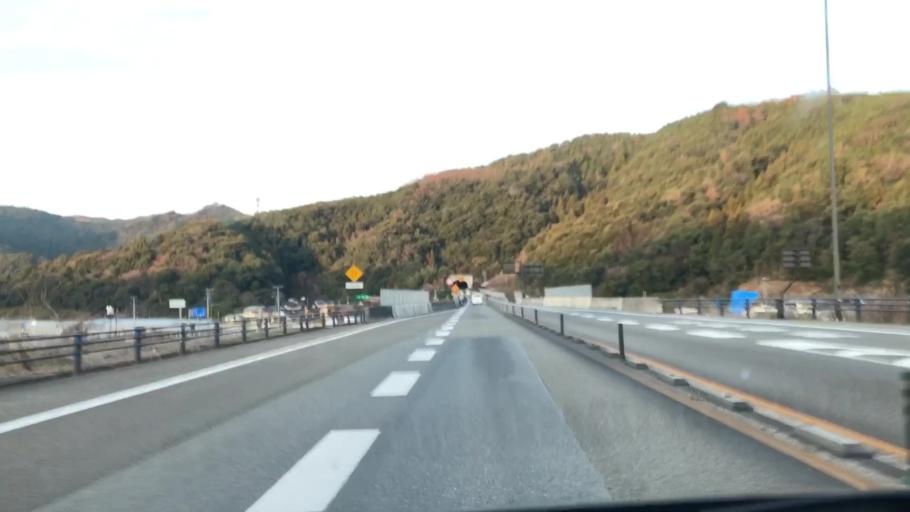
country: JP
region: Kumamoto
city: Minamata
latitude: 32.2994
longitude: 130.5096
